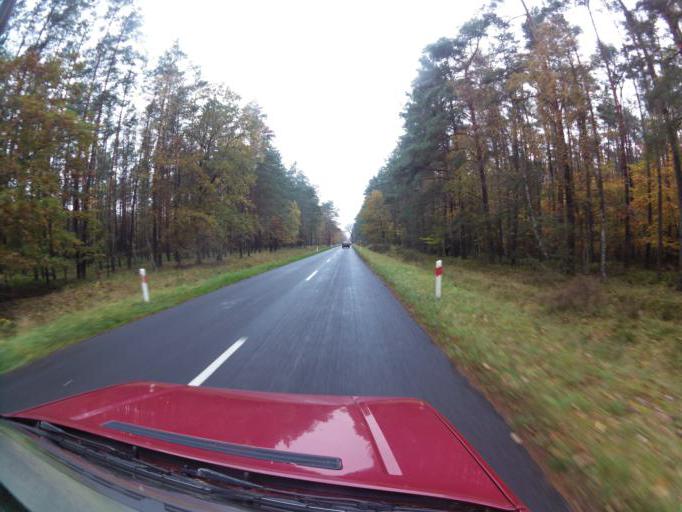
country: PL
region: West Pomeranian Voivodeship
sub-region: Powiat policki
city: Dobra
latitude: 53.5673
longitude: 14.4399
